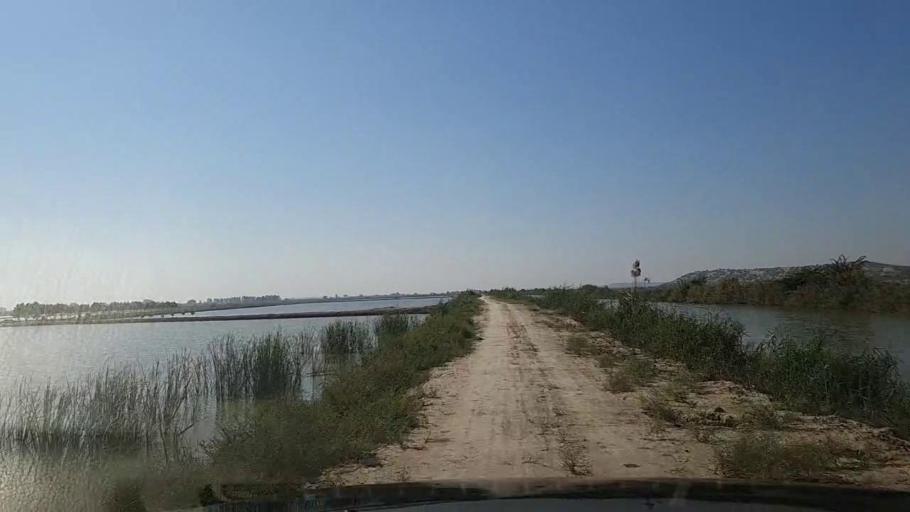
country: PK
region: Sindh
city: Thatta
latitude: 24.6823
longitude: 67.8911
